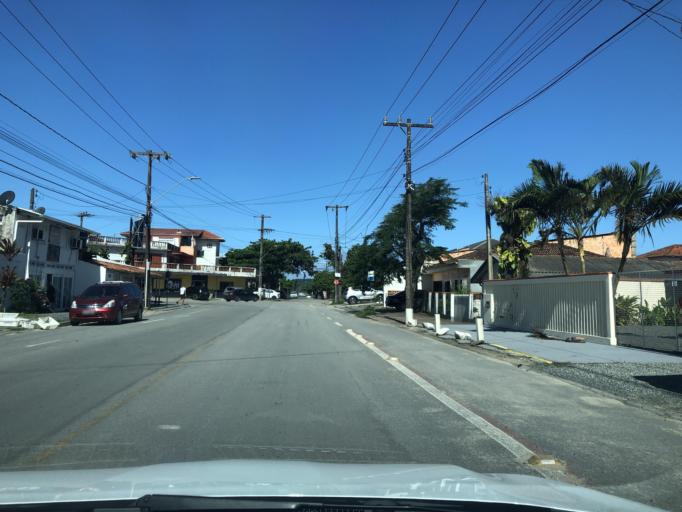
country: BR
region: Santa Catarina
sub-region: Sao Francisco Do Sul
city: Sao Francisco do Sul
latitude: -26.2230
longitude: -48.5224
